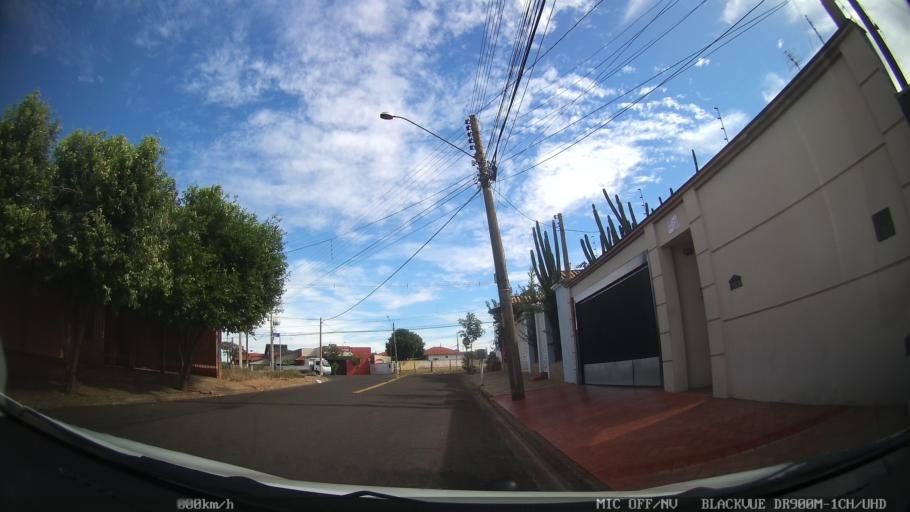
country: BR
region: Sao Paulo
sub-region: Catanduva
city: Catanduva
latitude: -21.1244
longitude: -48.9468
